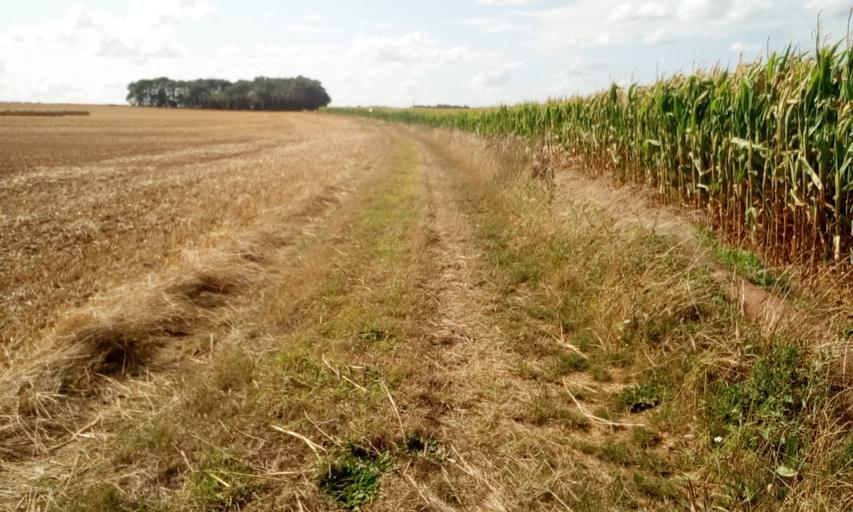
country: FR
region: Lower Normandy
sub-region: Departement du Calvados
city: Saint-Sylvain
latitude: 49.0712
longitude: -0.2433
